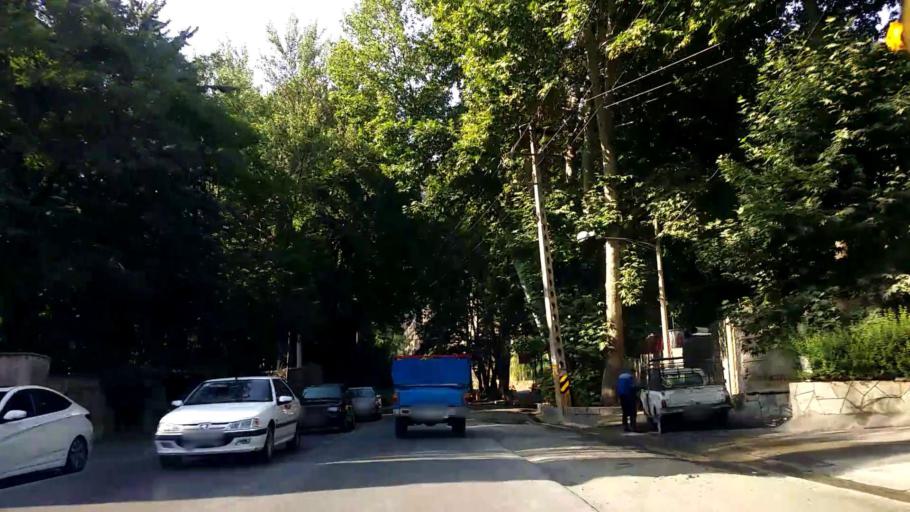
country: IR
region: Alborz
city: Karaj
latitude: 35.8821
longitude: 51.0416
